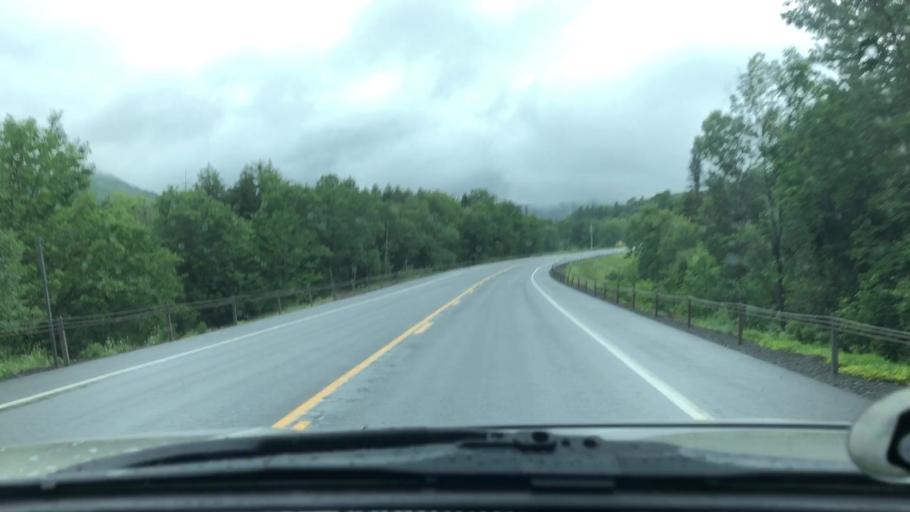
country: US
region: New York
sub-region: Greene County
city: Cairo
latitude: 42.3040
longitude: -74.2147
